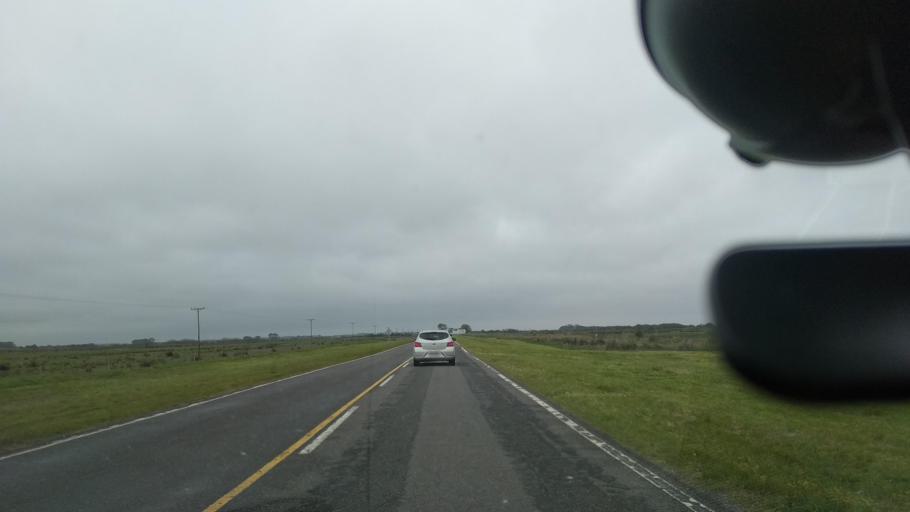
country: AR
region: Buenos Aires
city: Veronica
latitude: -35.6028
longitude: -57.2779
